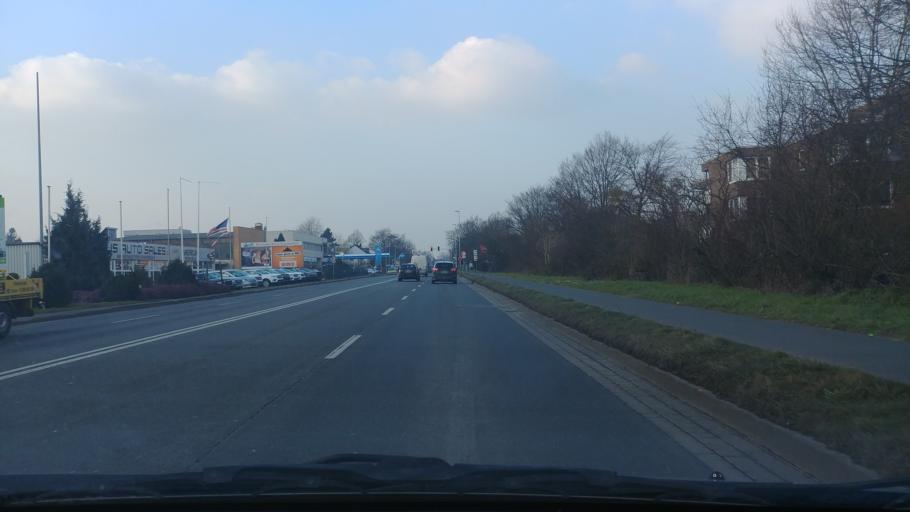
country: DE
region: Lower Saxony
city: Hemmingen
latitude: 52.3208
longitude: 9.7270
